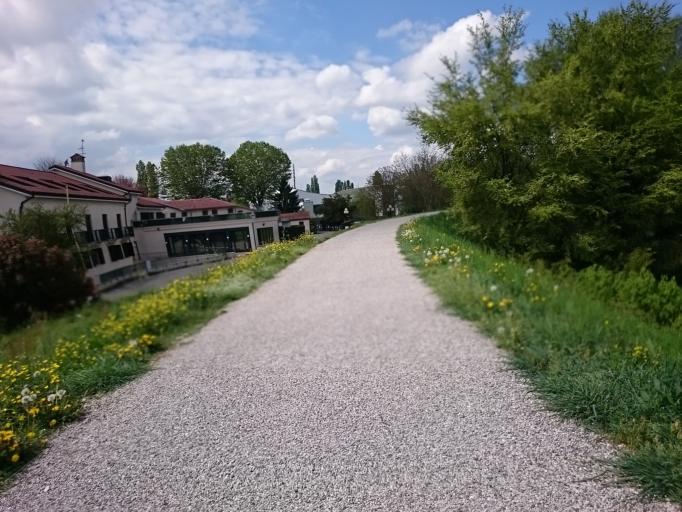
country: IT
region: Veneto
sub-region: Provincia di Padova
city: Tencarola
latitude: 45.3908
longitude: 11.8035
